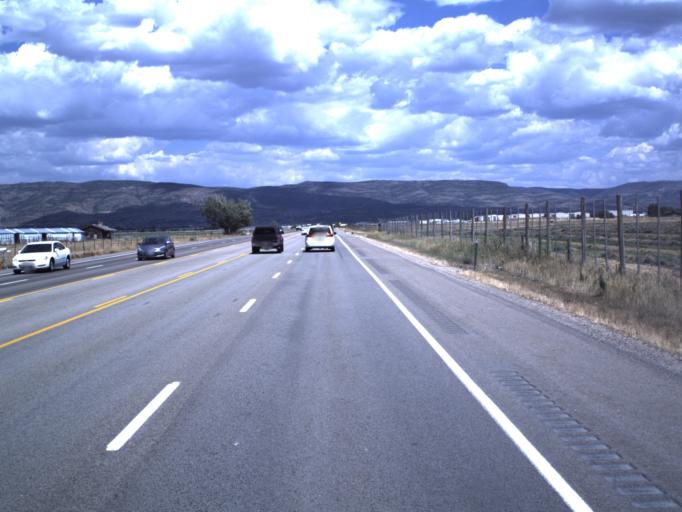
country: US
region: Utah
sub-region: Wasatch County
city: Heber
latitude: 40.4739
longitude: -111.4427
